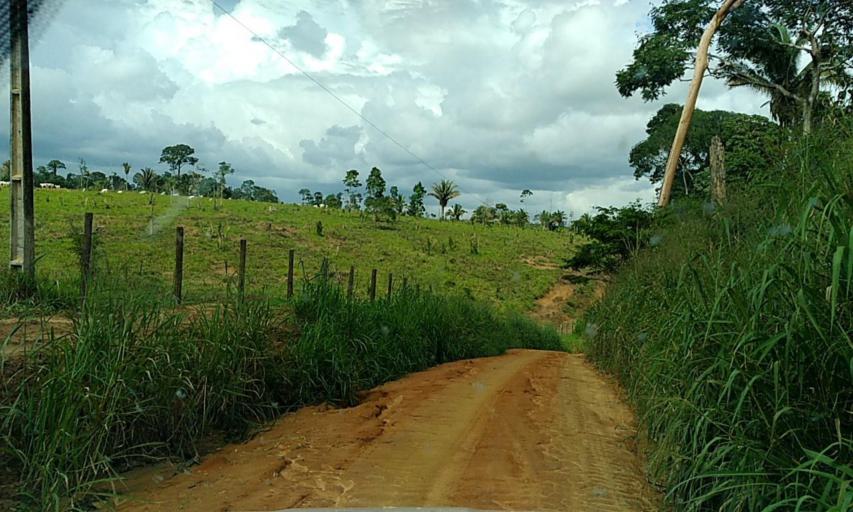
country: BR
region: Para
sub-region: Altamira
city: Altamira
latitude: -3.2330
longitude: -52.7333
